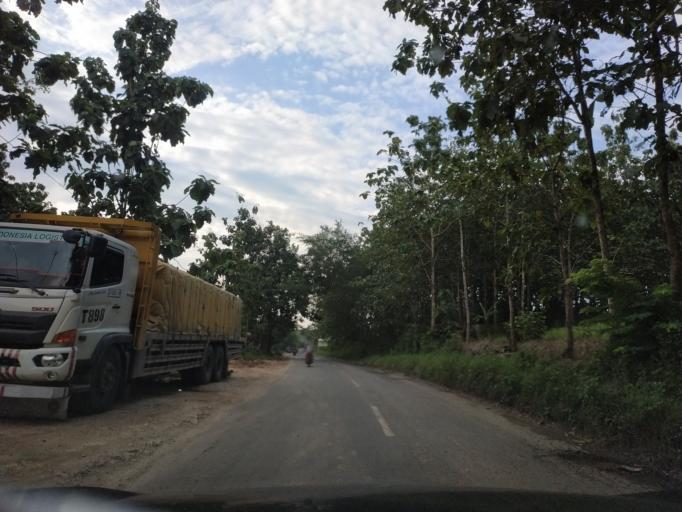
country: ID
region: Central Java
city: Ngampel
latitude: -6.8974
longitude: 111.4402
